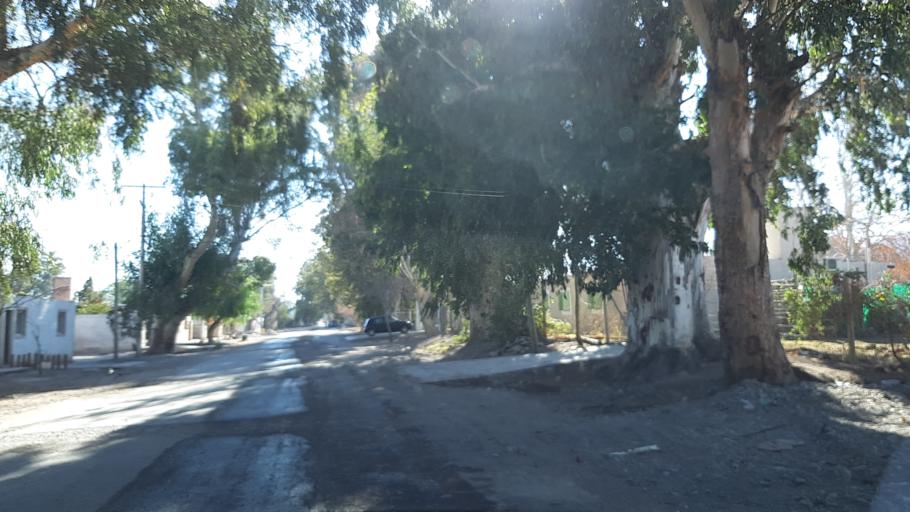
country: AR
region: San Juan
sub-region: Departamento de Zonda
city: Zonda
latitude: -31.5534
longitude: -68.7286
